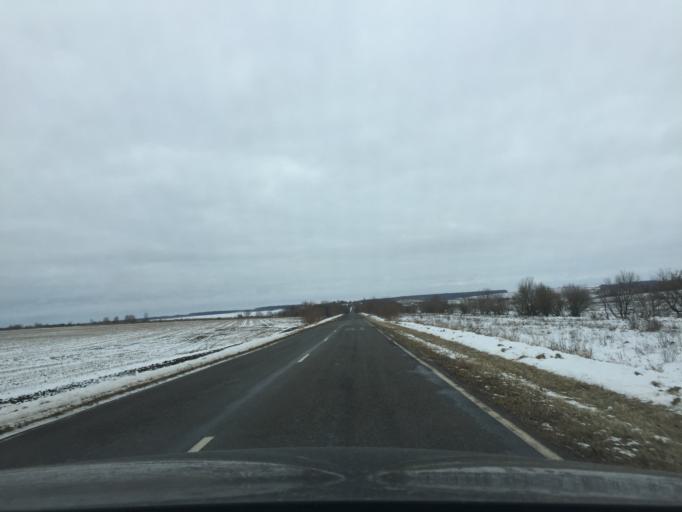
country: RU
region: Tula
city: Teploye
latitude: 53.7974
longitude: 37.5953
